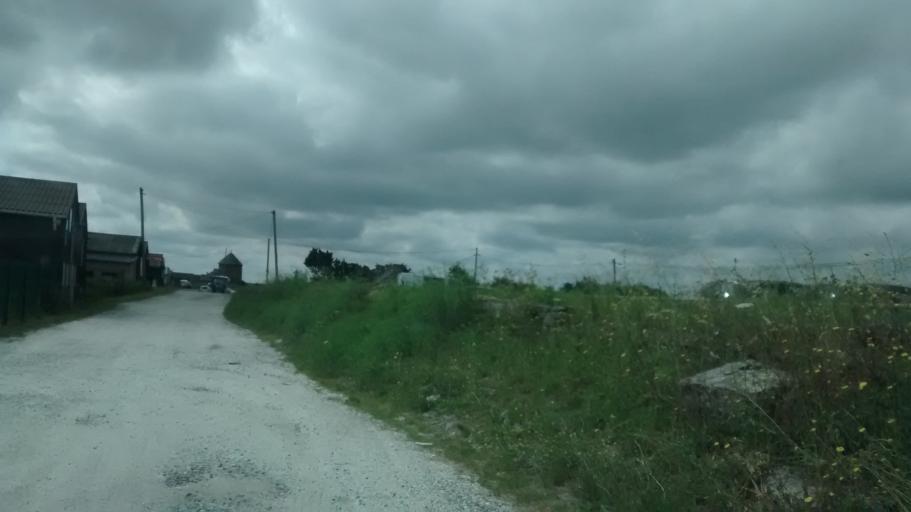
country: FR
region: Brittany
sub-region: Departement d'Ille-et-Vilaine
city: Saint-Meloir-des-Ondes
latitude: 48.6363
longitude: -1.8672
